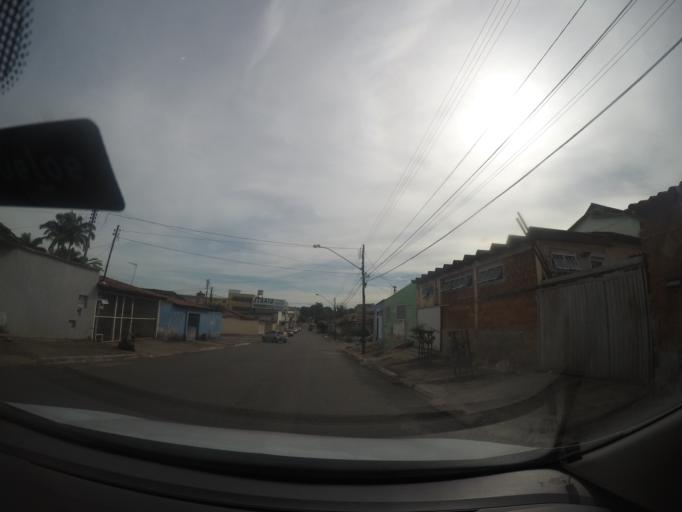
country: BR
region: Goias
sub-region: Goiania
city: Goiania
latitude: -16.6598
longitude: -49.3078
